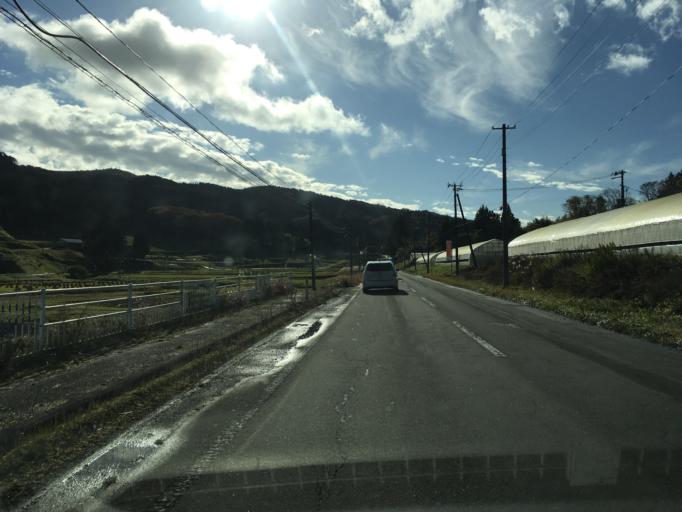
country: JP
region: Iwate
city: Ichinoseki
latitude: 38.9268
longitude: 141.4202
